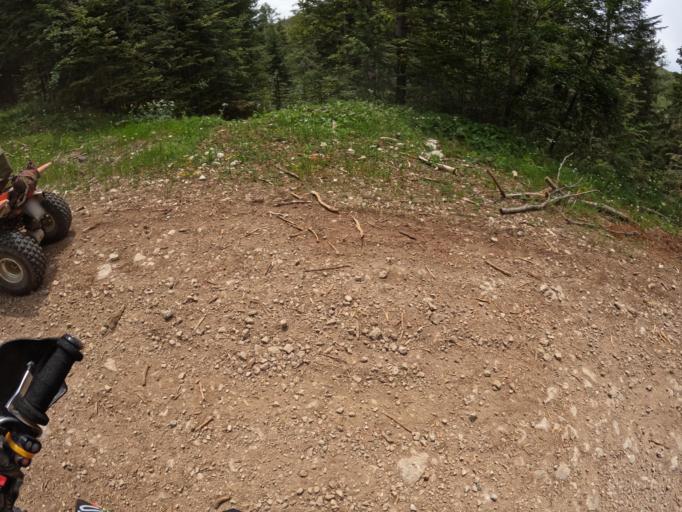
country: BA
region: Federation of Bosnia and Herzegovina
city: Glamoc
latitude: 44.1272
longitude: 16.6420
